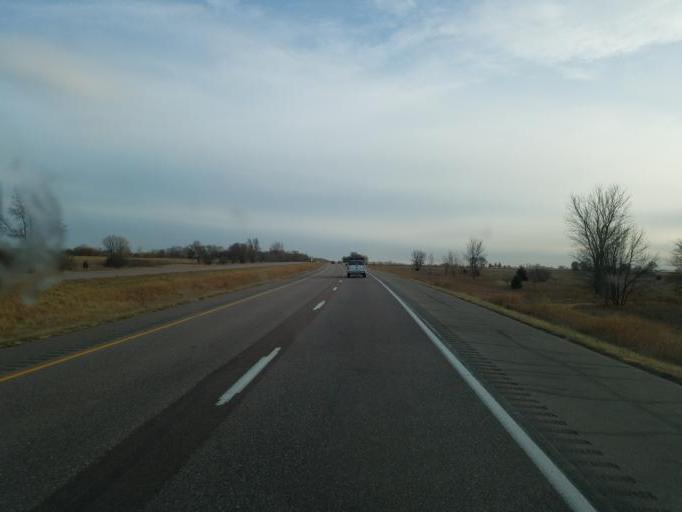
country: US
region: Nebraska
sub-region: Thurston County
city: Macy
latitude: 42.1555
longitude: -96.2226
